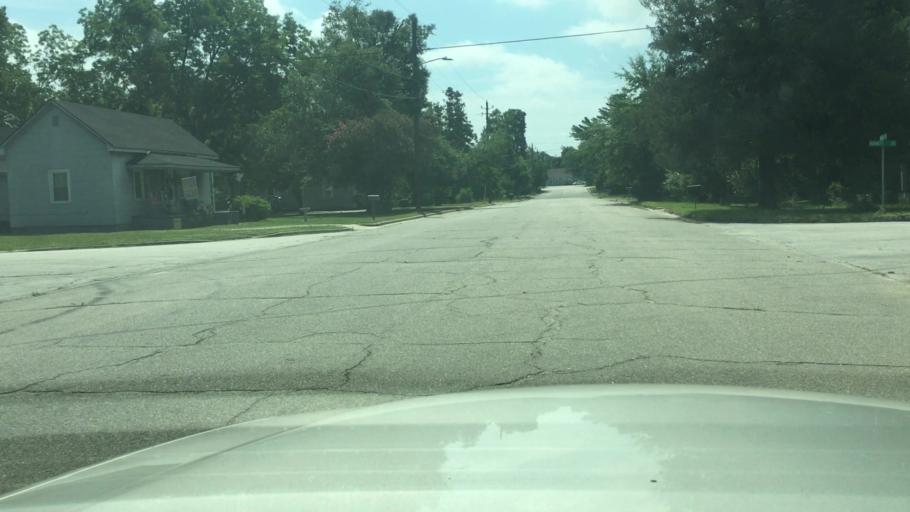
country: US
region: North Carolina
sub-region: Cumberland County
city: Fayetteville
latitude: 35.0255
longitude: -78.9030
